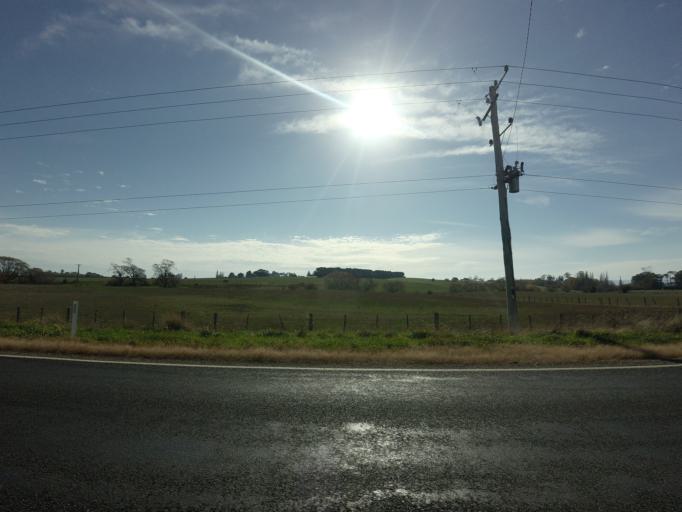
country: AU
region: Tasmania
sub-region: Meander Valley
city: Westbury
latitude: -41.5288
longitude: 146.9266
